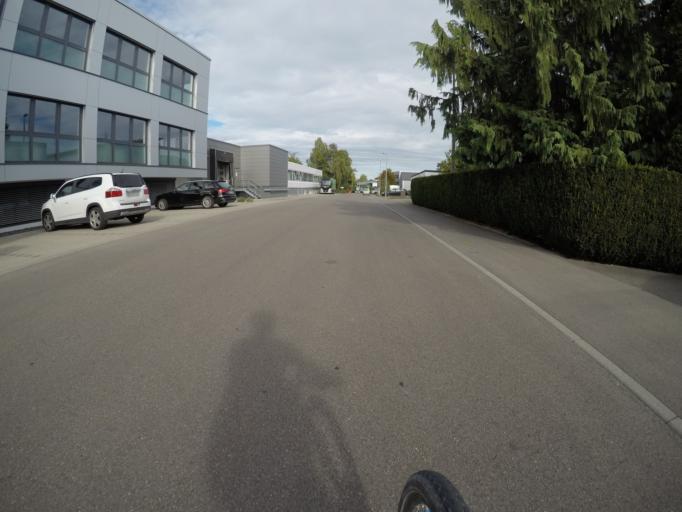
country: DE
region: Baden-Wuerttemberg
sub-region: Regierungsbezirk Stuttgart
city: Freiberg am Neckar
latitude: 48.9091
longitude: 9.2315
